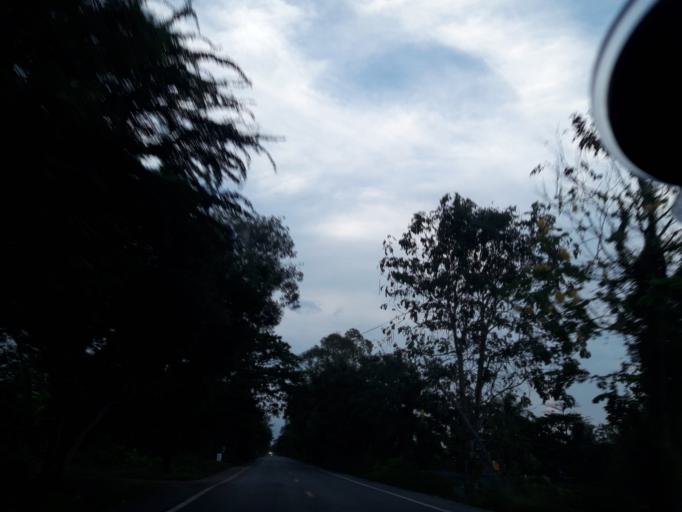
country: TH
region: Pathum Thani
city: Nong Suea
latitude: 14.1510
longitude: 100.8690
